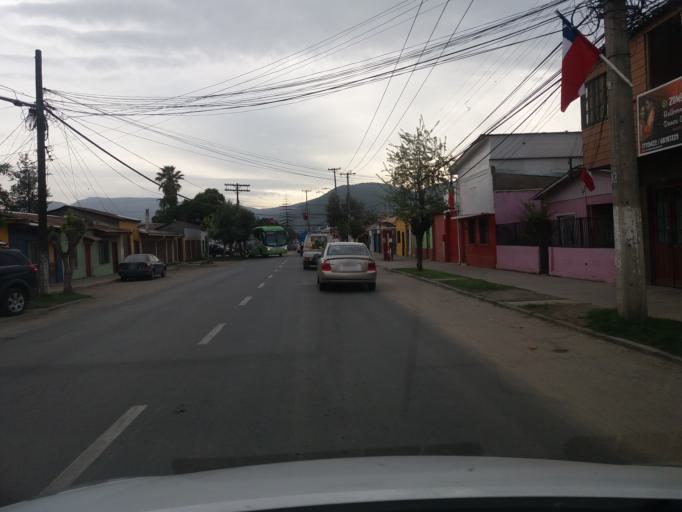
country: CL
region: Valparaiso
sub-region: Provincia de Quillota
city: Hacienda La Calera
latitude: -32.7779
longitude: -71.1905
